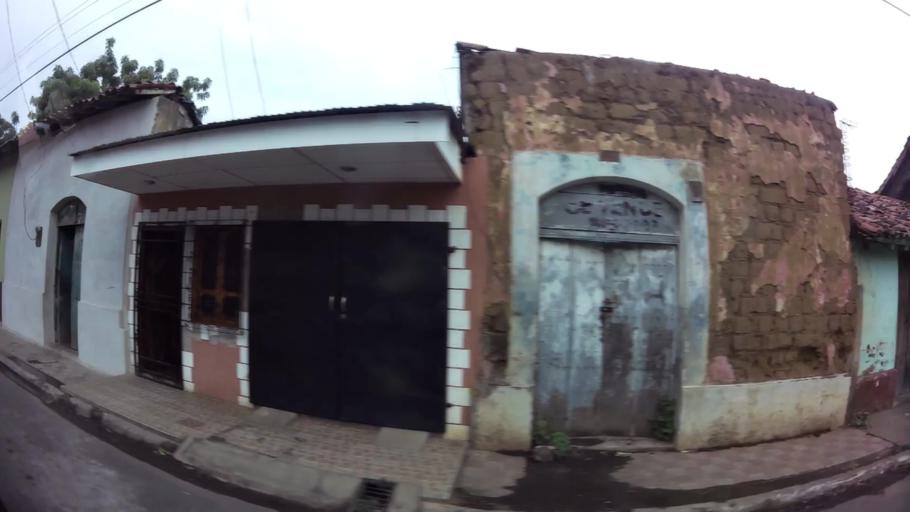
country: NI
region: Leon
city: Leon
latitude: 12.4432
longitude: -86.8784
